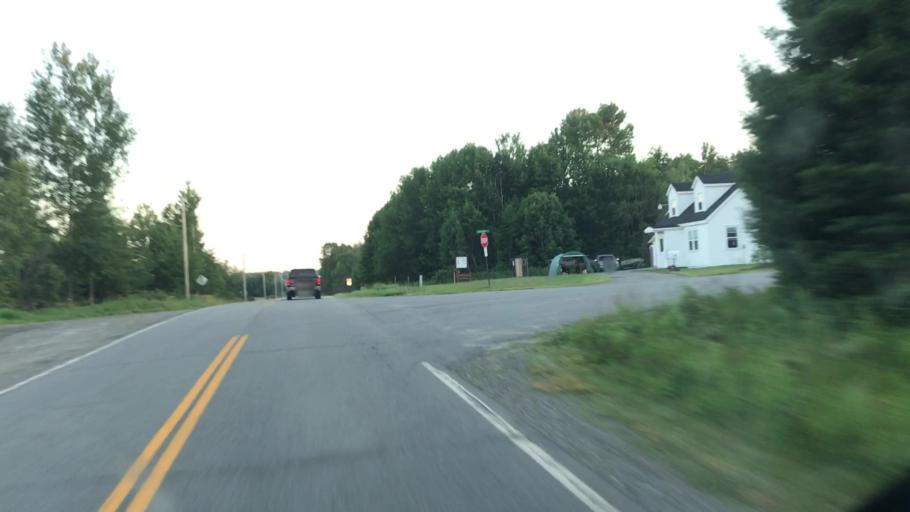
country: US
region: Maine
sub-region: Penobscot County
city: Medway
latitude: 45.6156
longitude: -68.3034
